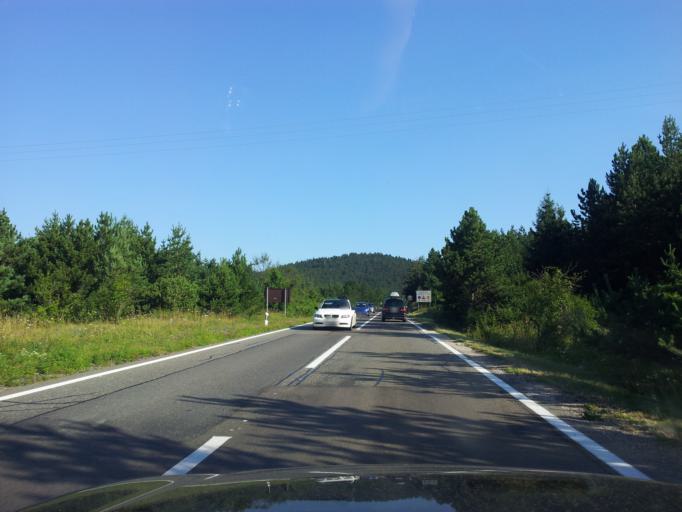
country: HR
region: Licko-Senjska
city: Jezerce
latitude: 44.7823
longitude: 15.6882
